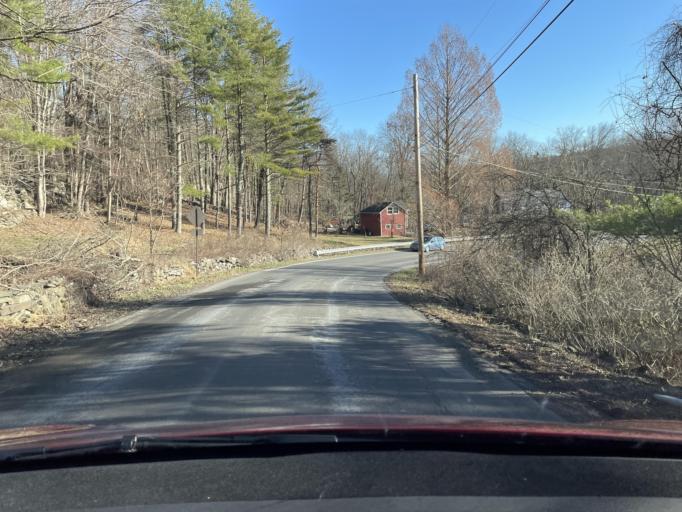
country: US
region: New York
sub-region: Ulster County
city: Zena
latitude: 42.0460
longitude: -74.0165
